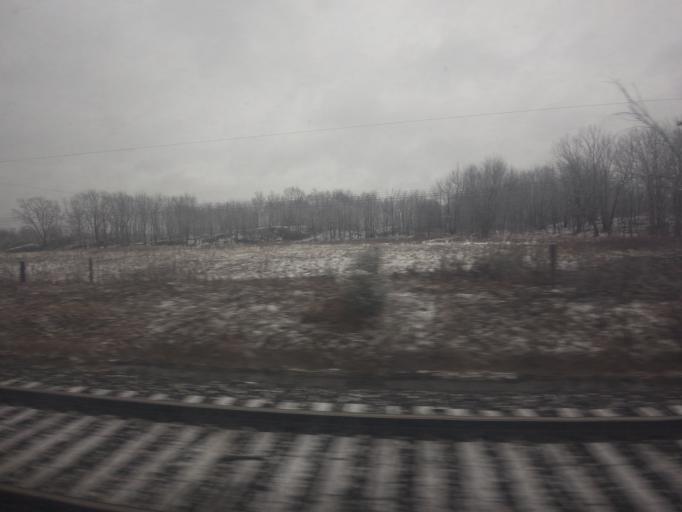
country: US
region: New York
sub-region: Jefferson County
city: Alexandria Bay
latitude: 44.4509
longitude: -75.9349
